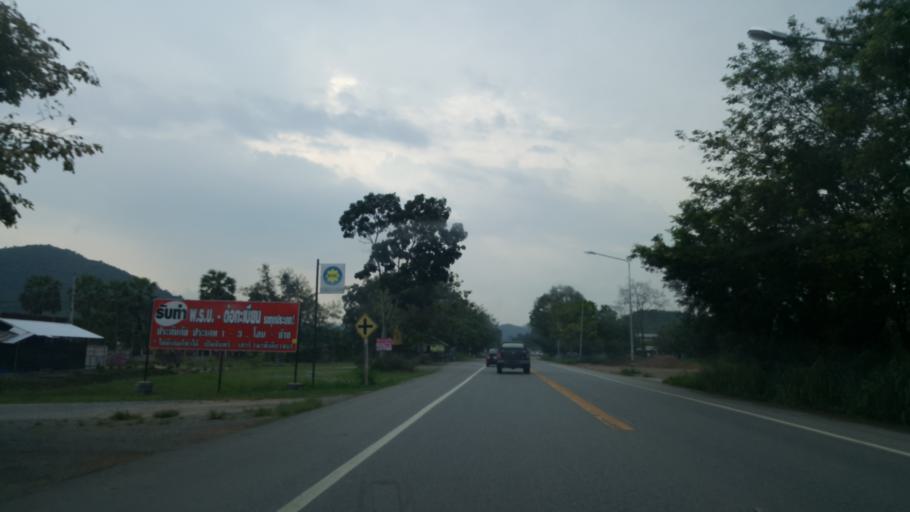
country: TH
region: Rayong
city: Ban Chang
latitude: 12.7270
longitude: 100.9722
